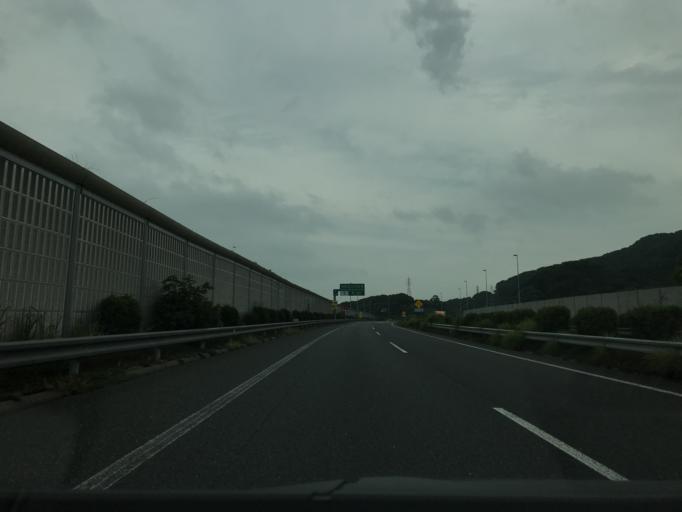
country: JP
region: Fukuoka
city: Kanda
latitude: 33.7974
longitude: 130.9630
